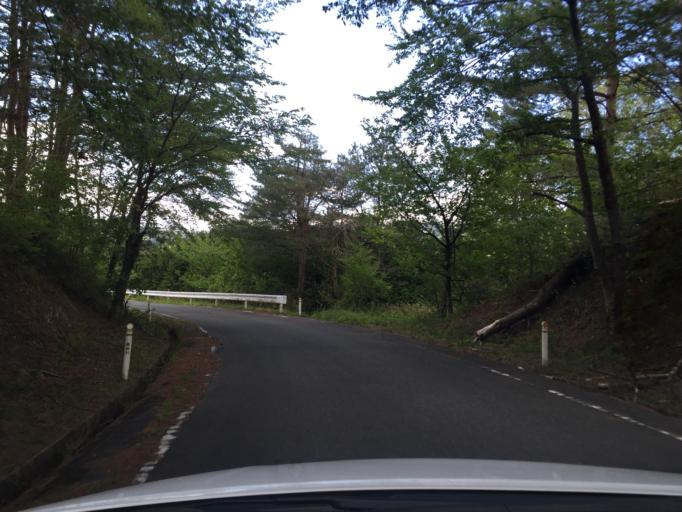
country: JP
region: Miyagi
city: Marumori
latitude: 37.7199
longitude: 140.8227
